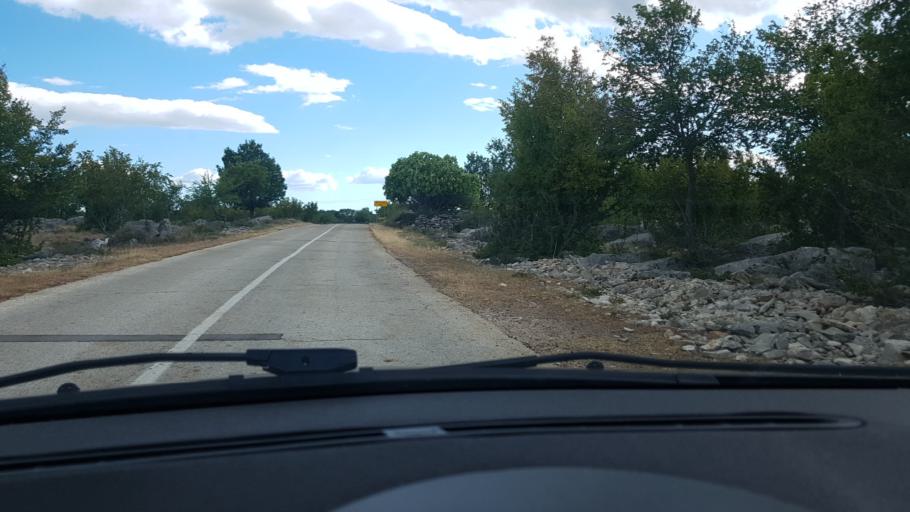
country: HR
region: Sibensko-Kniniska
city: Kistanje
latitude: 44.0624
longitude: 15.9323
